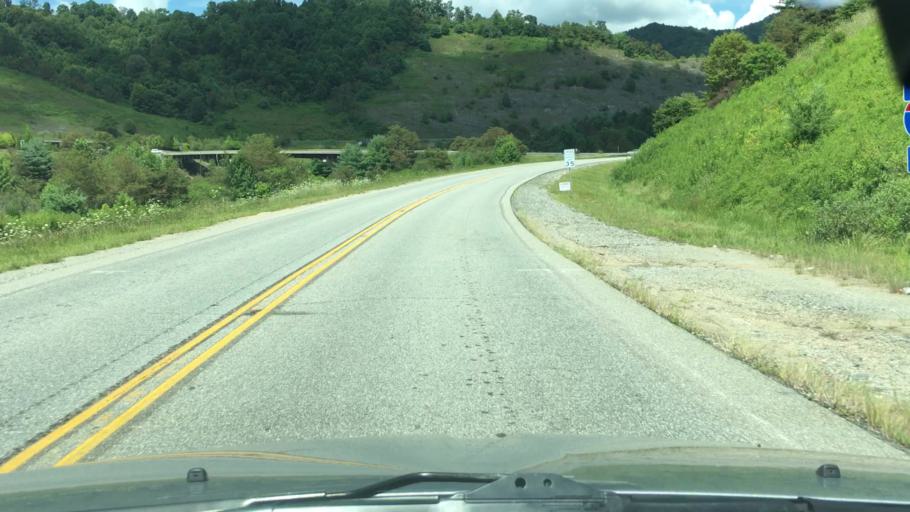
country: US
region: North Carolina
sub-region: Madison County
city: Mars Hill
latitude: 35.9086
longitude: -82.5537
